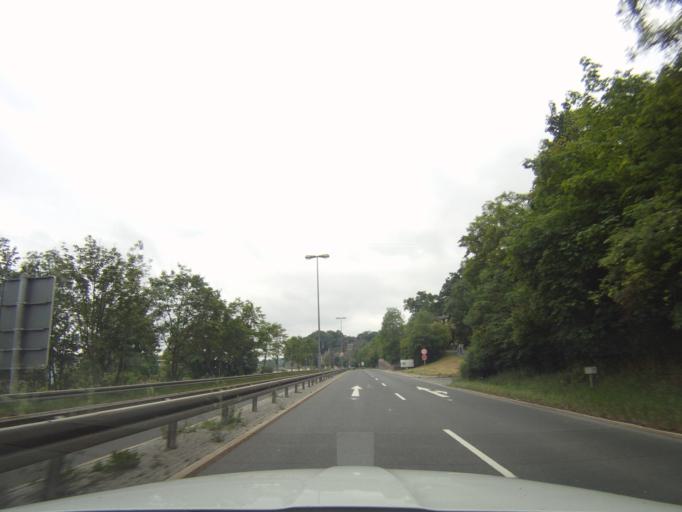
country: DE
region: Bavaria
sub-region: Upper Franconia
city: Coburg
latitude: 50.2670
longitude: 10.9558
